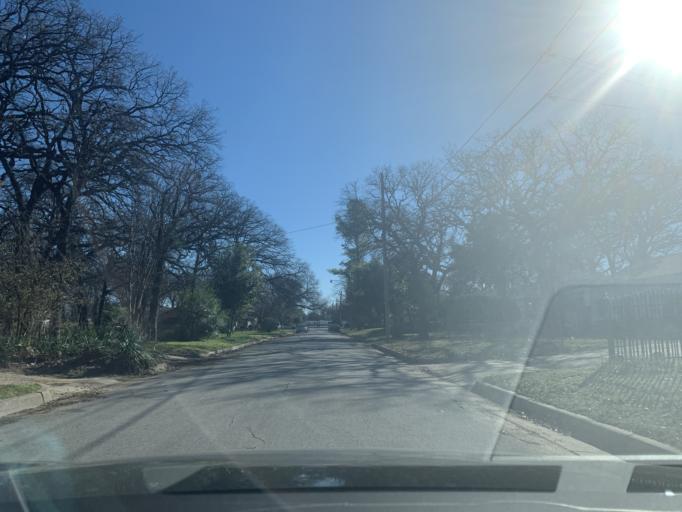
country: US
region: Texas
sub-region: Tarrant County
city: Haltom City
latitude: 32.7790
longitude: -97.2842
